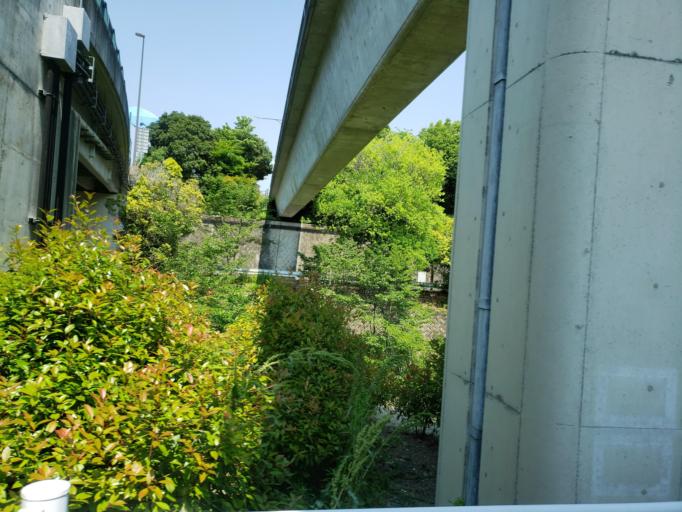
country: JP
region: Tokushima
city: Ikedacho
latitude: 34.0369
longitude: 133.8931
